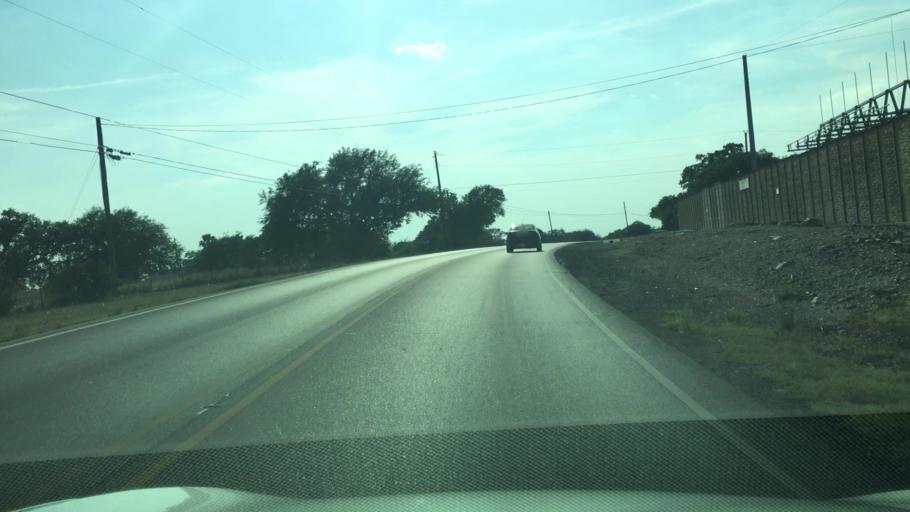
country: US
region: Texas
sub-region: Hays County
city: Dripping Springs
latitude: 30.1172
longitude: -97.9852
